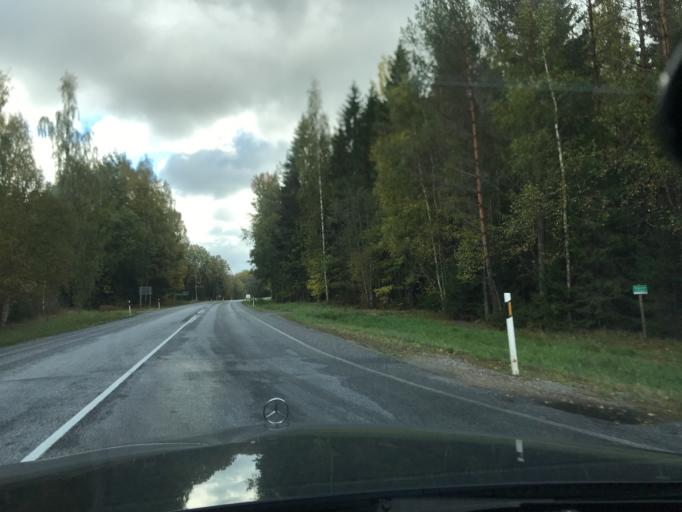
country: EE
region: Vorumaa
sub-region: Voru linn
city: Voru
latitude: 57.7274
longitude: 27.3104
